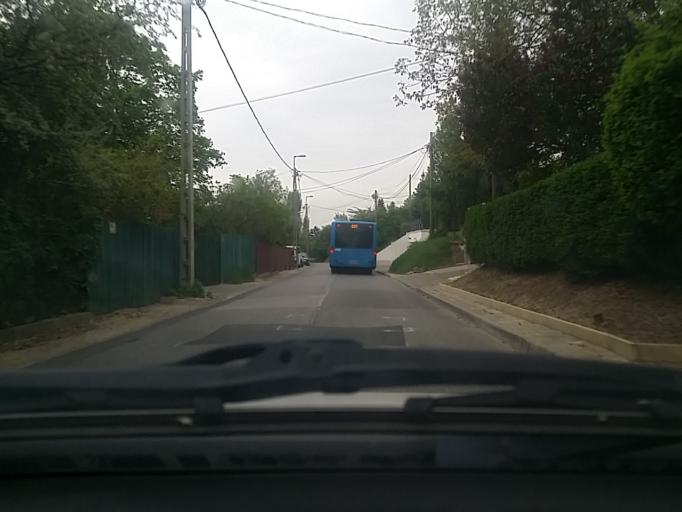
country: HU
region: Pest
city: Urom
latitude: 47.5598
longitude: 19.0118
